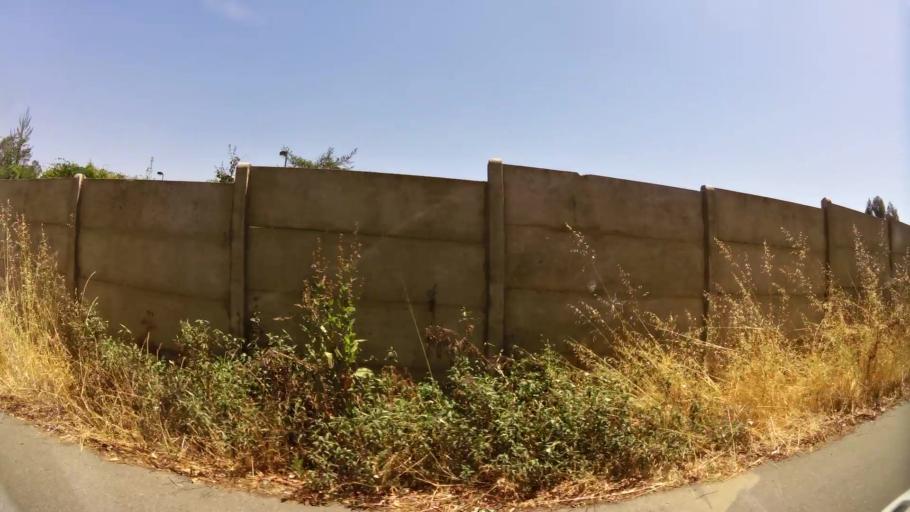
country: CL
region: Maule
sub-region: Provincia de Curico
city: Curico
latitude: -34.9972
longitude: -71.2076
